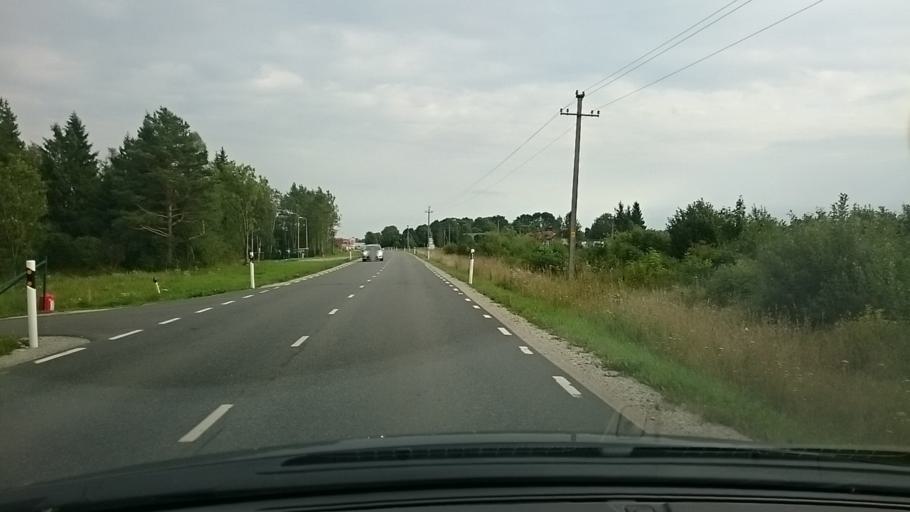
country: EE
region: Harju
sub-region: Harku vald
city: Tabasalu
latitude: 59.4233
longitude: 24.5347
